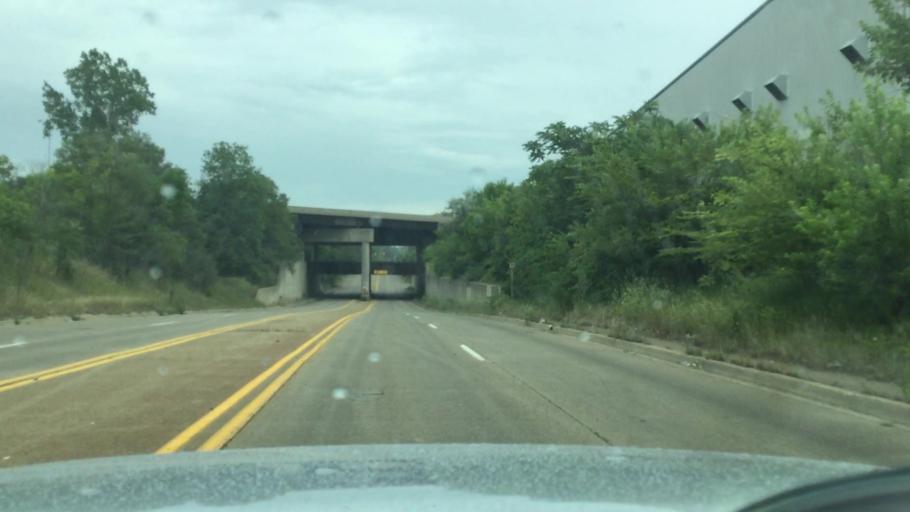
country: US
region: Michigan
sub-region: Genesee County
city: Beecher
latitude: 43.0613
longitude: -83.6799
